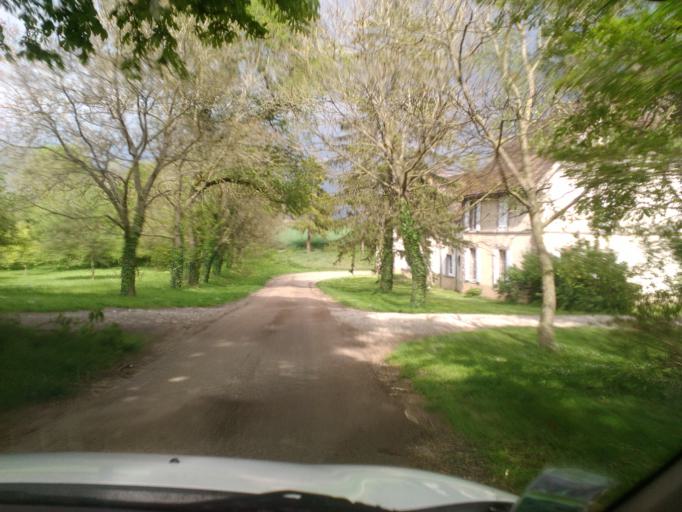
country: FR
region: Champagne-Ardenne
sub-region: Departement de l'Aube
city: Nogent-sur-Seine
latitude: 48.3802
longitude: 3.4993
